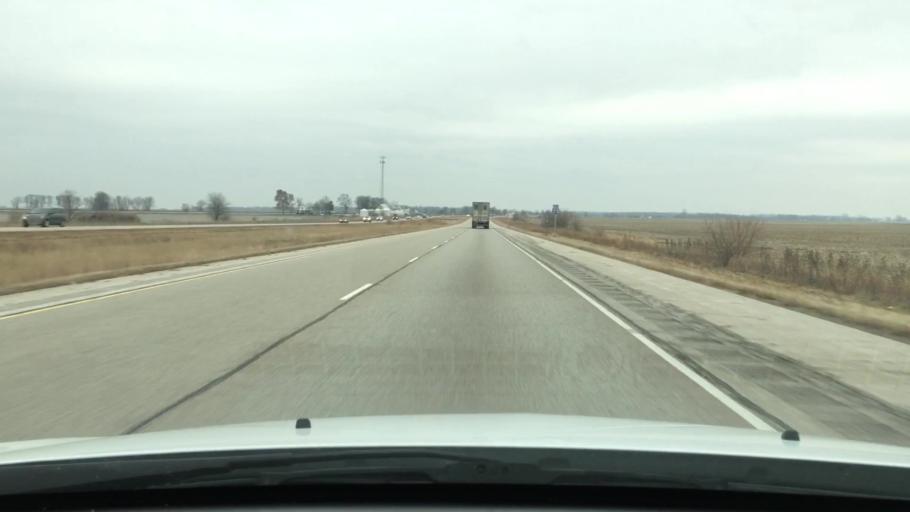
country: US
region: Illinois
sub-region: Logan County
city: Atlanta
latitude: 40.3177
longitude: -89.1589
